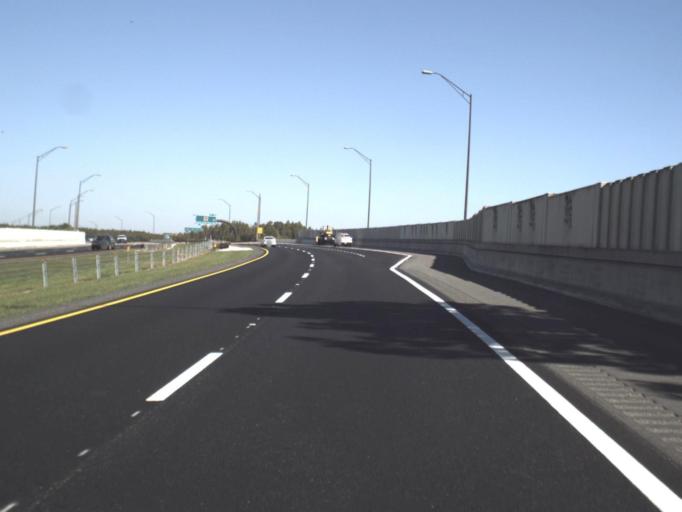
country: US
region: Florida
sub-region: Hillsborough County
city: Cheval
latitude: 28.1541
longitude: -82.5381
